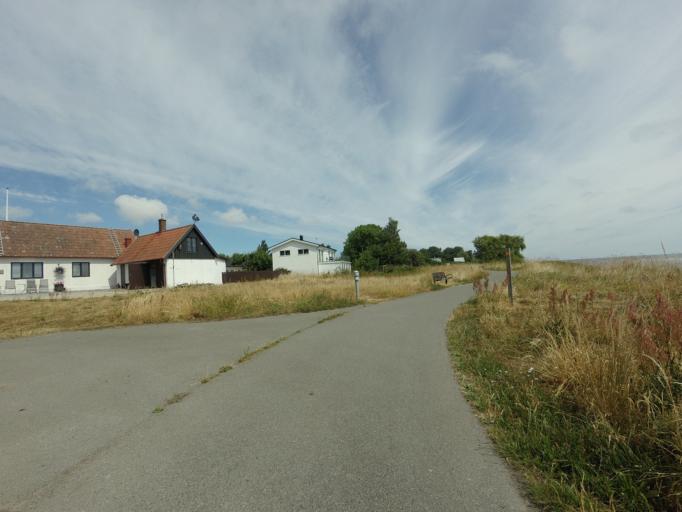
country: SE
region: Skane
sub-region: Simrishamns Kommun
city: Simrishamn
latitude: 55.5247
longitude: 14.3475
